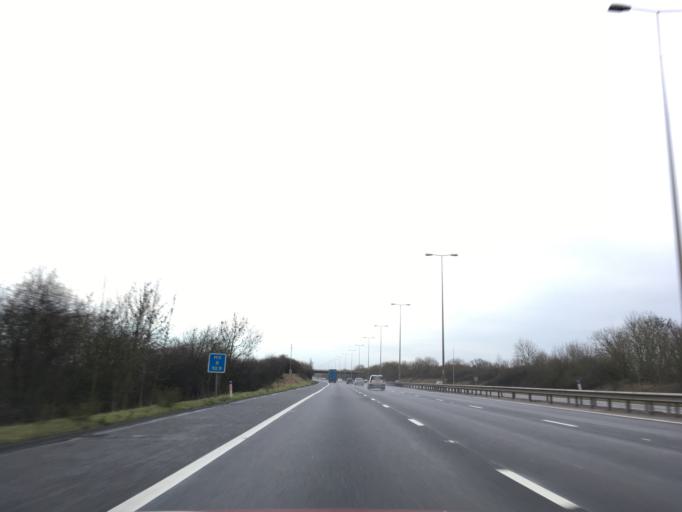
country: GB
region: England
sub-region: Worcestershire
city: Kempsey
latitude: 52.1355
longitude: -2.1989
